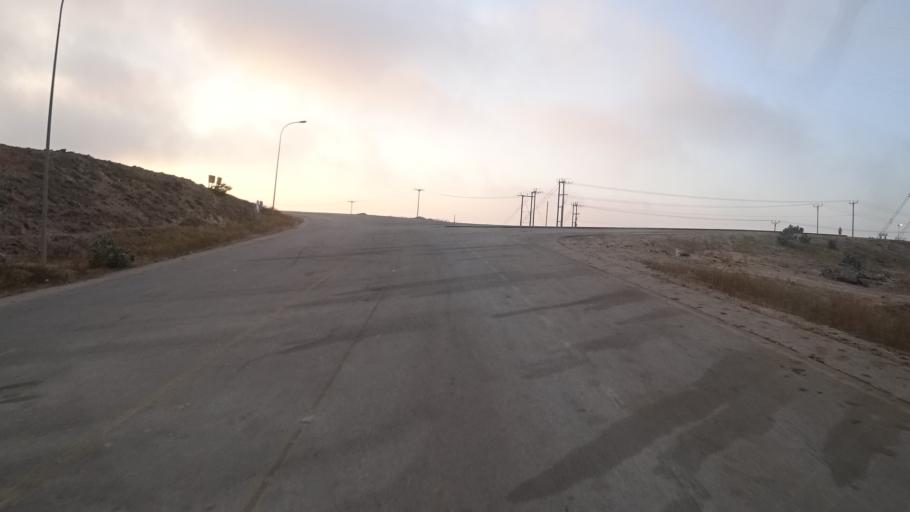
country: OM
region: Zufar
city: Salalah
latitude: 17.1222
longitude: 53.9274
